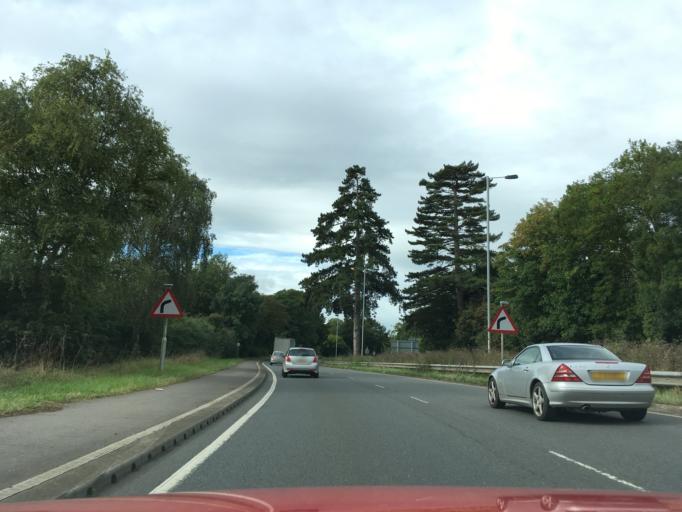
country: GB
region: England
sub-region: Gloucestershire
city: Gloucester
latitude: 51.8721
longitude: -2.2901
